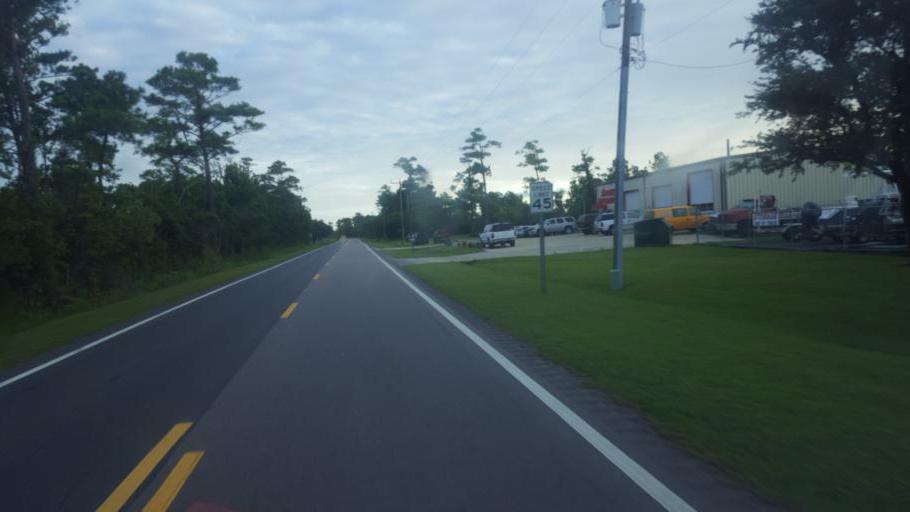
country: US
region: North Carolina
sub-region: Dare County
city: Manteo
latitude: 35.8826
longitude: -75.6592
